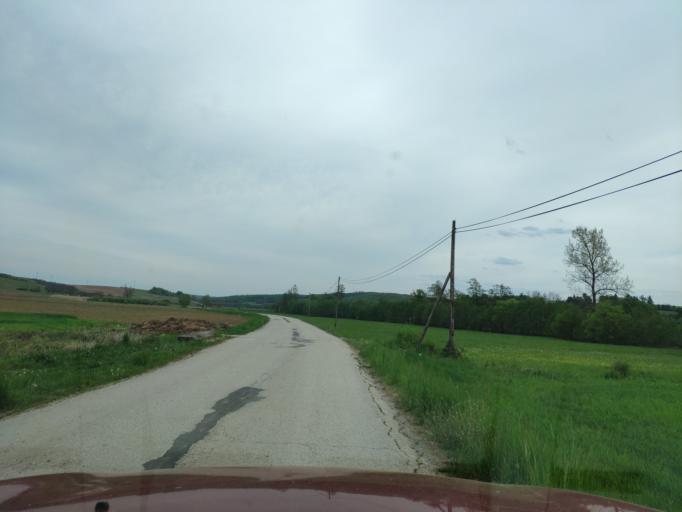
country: SK
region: Banskobystricky
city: Revuca
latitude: 48.4977
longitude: 20.2084
